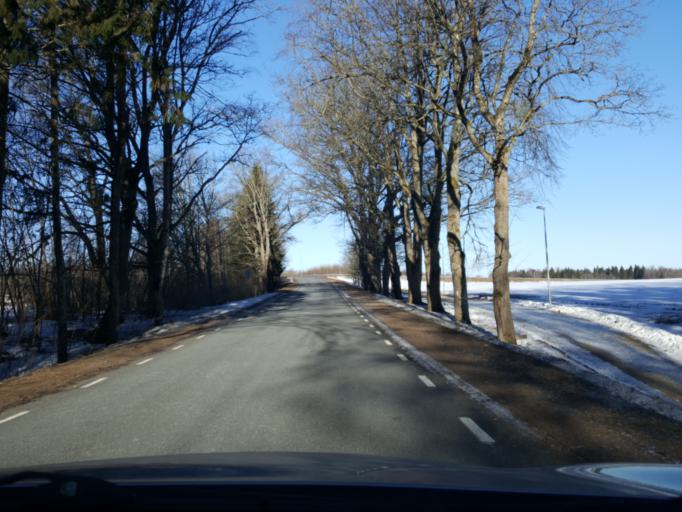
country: EE
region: Viljandimaa
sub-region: Vohma linn
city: Vohma
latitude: 58.5598
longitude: 25.5537
